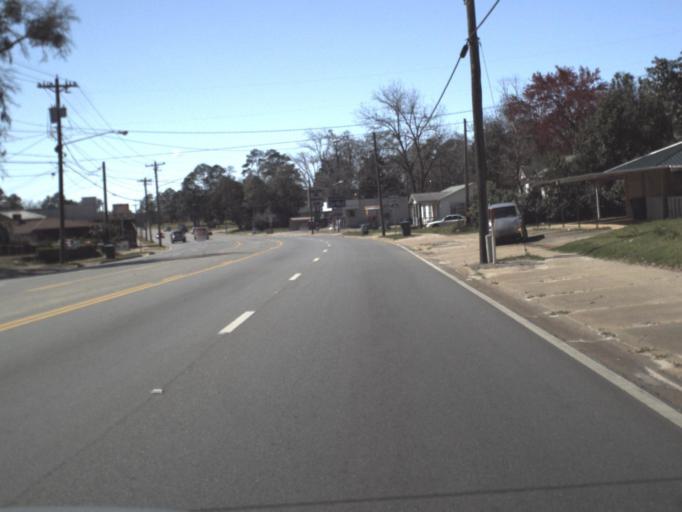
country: US
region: Florida
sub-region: Gadsden County
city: Quincy
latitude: 30.5856
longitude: -84.6027
